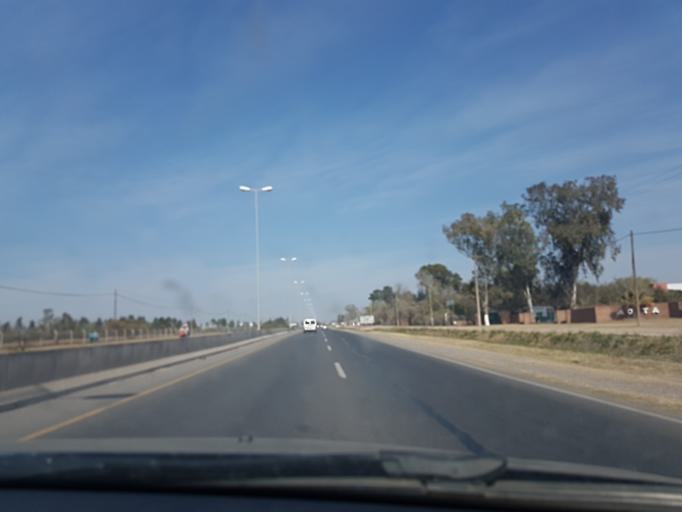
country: AR
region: Cordoba
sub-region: Departamento de Capital
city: Cordoba
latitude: -31.4896
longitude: -64.2501
